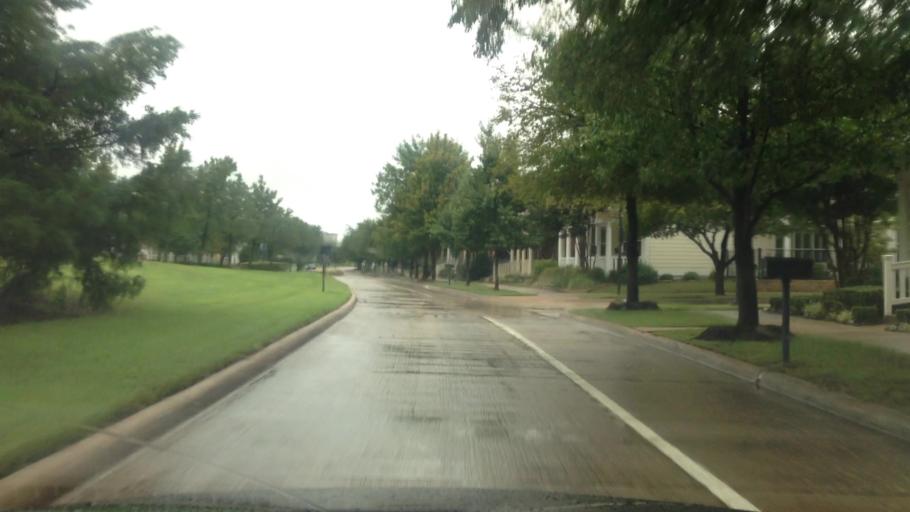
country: US
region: Texas
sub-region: Tarrant County
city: North Richland Hills
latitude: 32.8555
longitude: -97.2019
